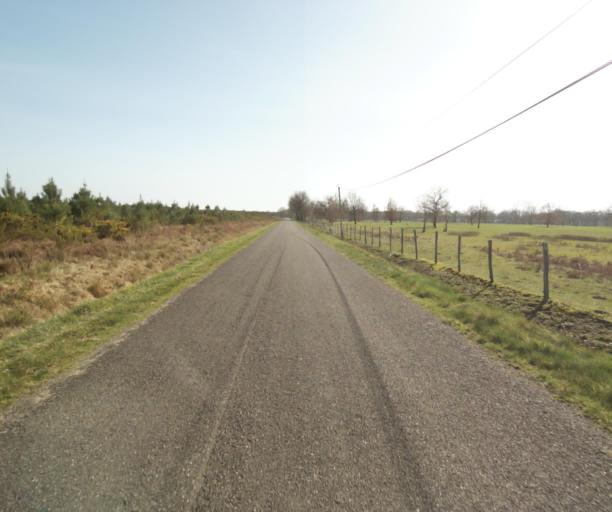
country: FR
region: Aquitaine
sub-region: Departement des Landes
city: Roquefort
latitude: 44.1396
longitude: -0.2628
